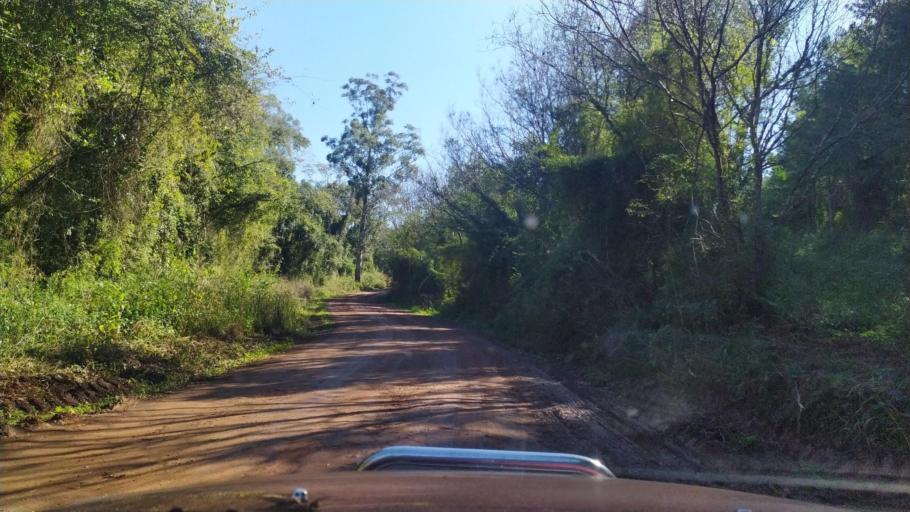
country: AR
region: Misiones
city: El Alcazar
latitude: -26.7290
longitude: -54.6785
